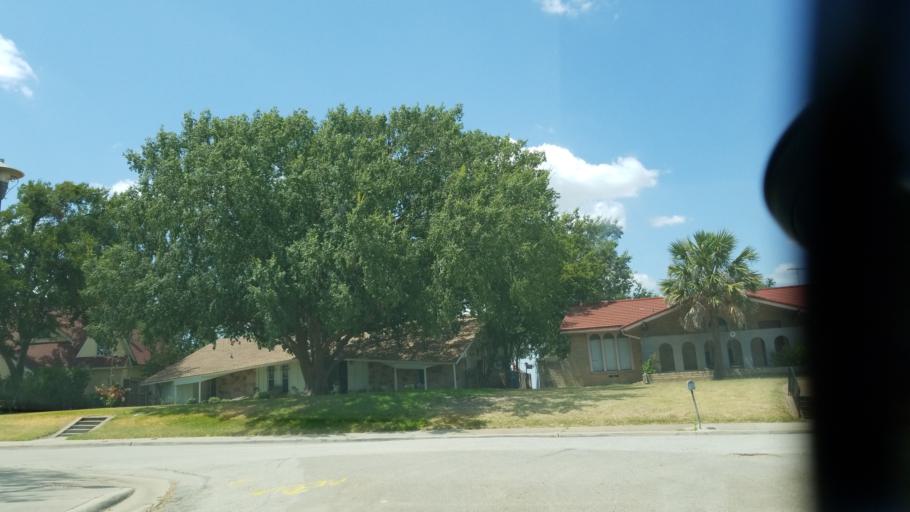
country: US
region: Texas
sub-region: Dallas County
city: Cockrell Hill
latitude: 32.7353
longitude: -96.9285
